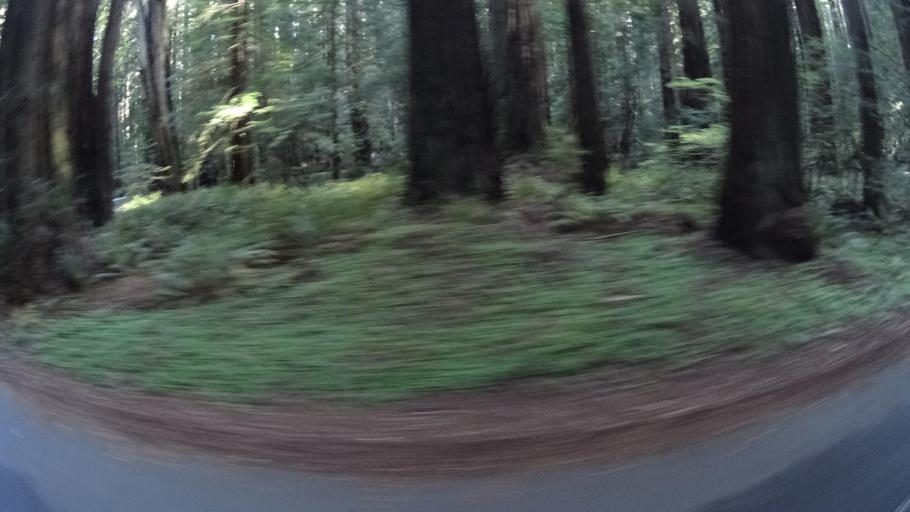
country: US
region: California
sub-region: Humboldt County
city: Rio Dell
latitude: 40.3516
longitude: -124.0025
